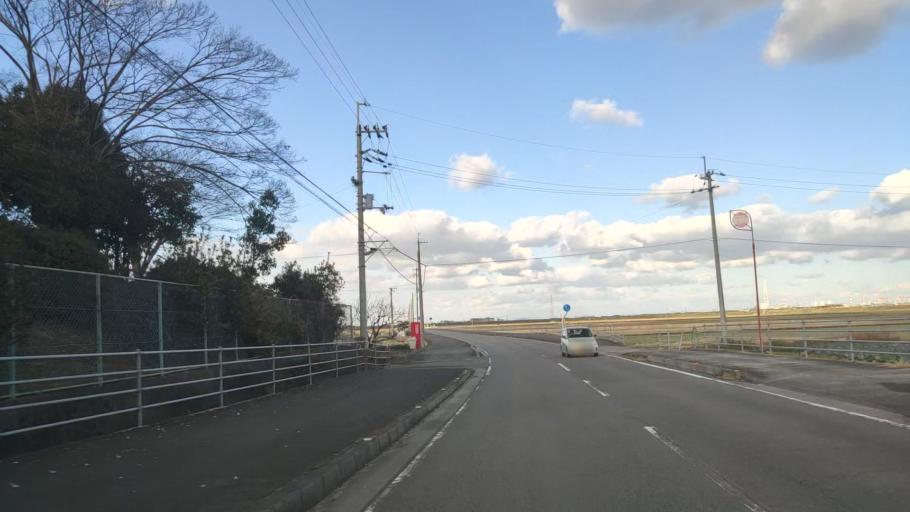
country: JP
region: Ehime
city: Saijo
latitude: 33.8993
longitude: 133.1350
